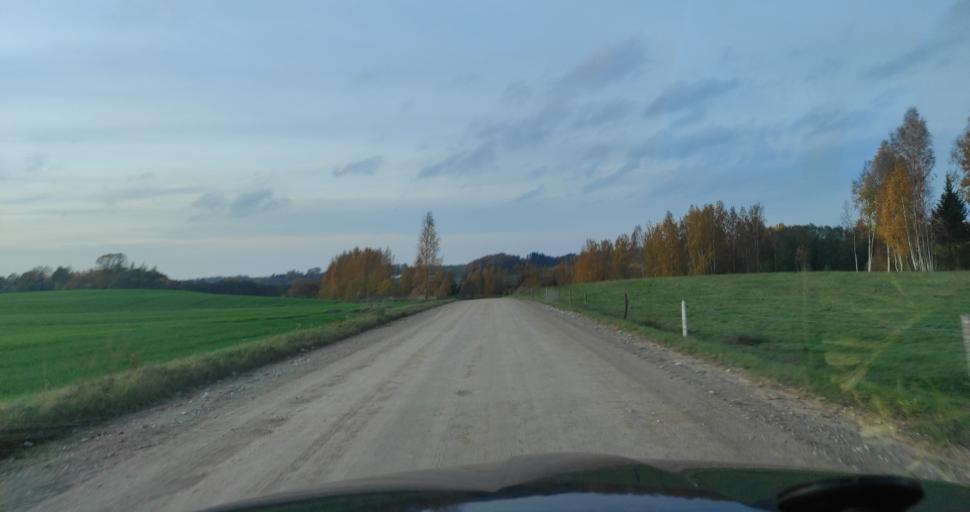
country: LV
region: Skrunda
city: Skrunda
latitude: 56.6431
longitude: 21.8043
